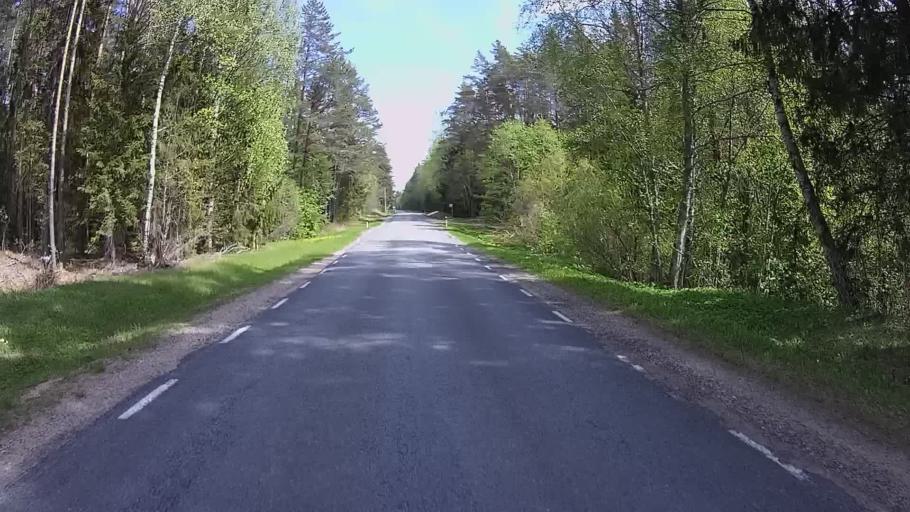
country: LV
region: Apes Novads
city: Ape
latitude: 57.6026
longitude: 26.5049
